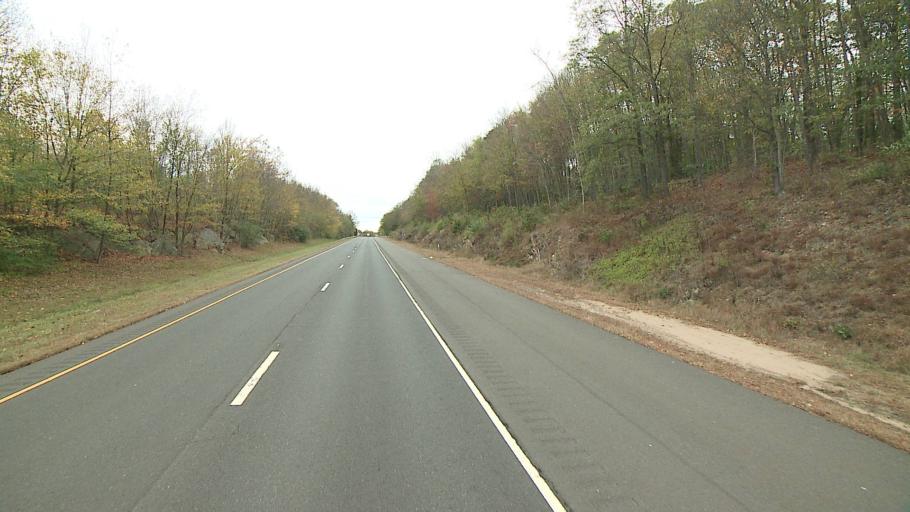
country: US
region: Connecticut
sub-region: Middlesex County
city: East Haddam
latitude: 41.4306
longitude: -72.5095
